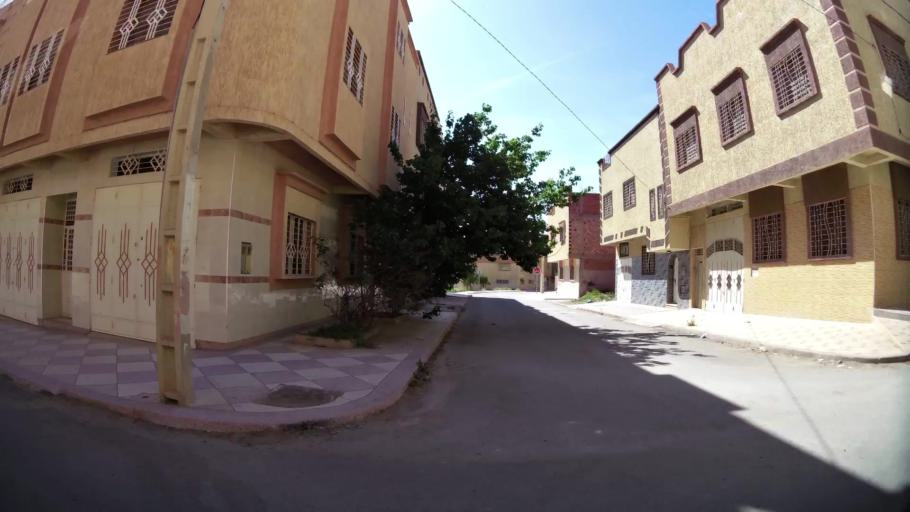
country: MA
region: Oriental
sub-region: Oujda-Angad
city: Oujda
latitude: 34.6578
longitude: -1.9187
